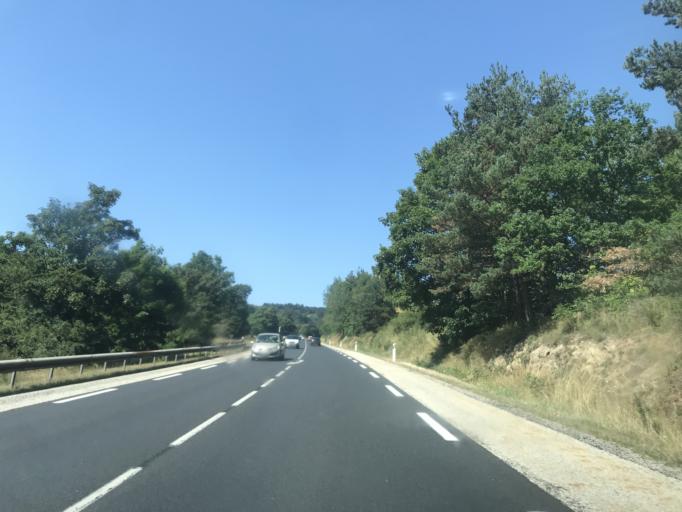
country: FR
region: Auvergne
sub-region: Departement de la Haute-Loire
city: Allegre
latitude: 45.1242
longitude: 3.7099
